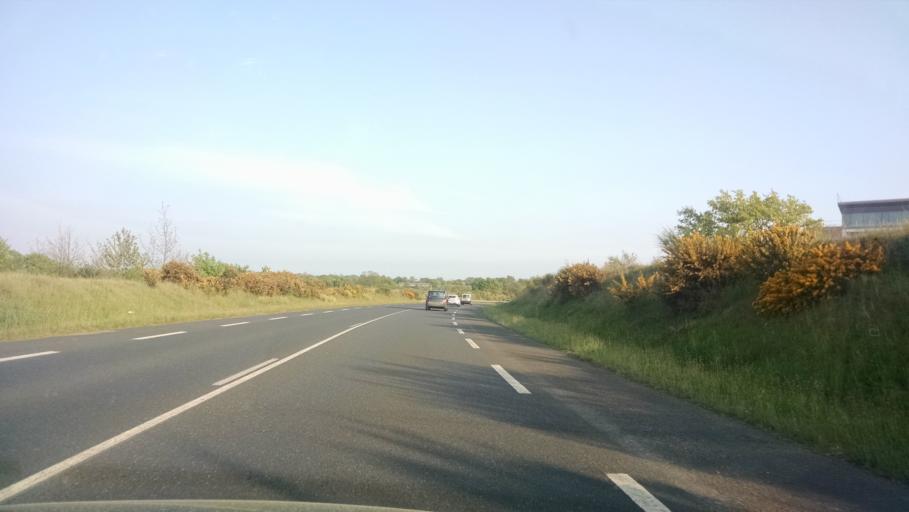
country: FR
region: Pays de la Loire
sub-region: Departement de la Loire-Atlantique
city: Clisson
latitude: 47.0948
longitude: -1.2675
